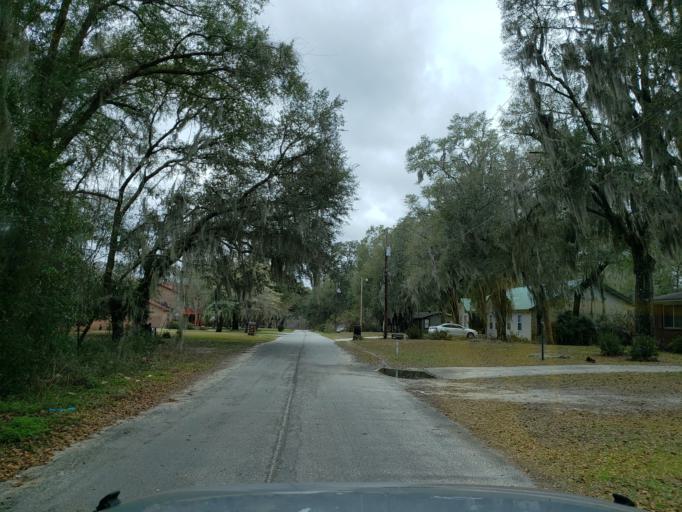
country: US
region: Georgia
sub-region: Chatham County
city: Bloomingdale
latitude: 32.0750
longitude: -81.3706
